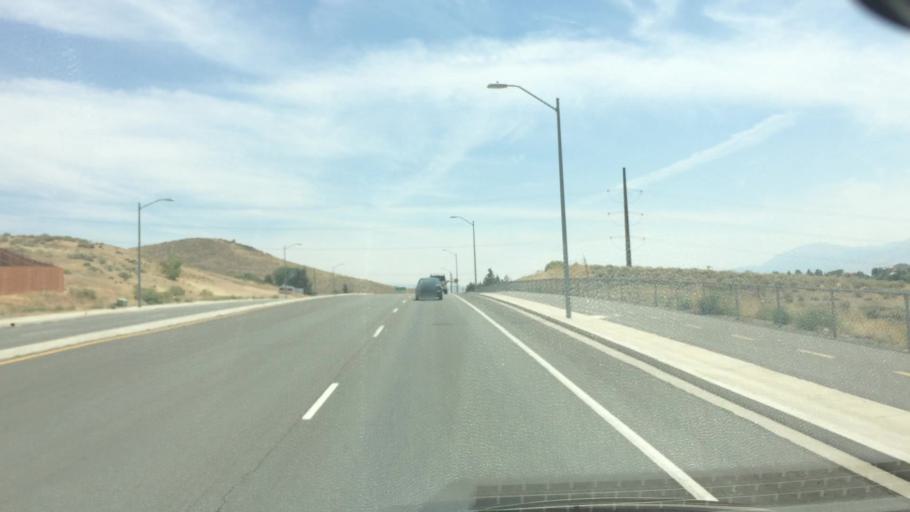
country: US
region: Nevada
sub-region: Washoe County
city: Sparks
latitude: 39.5729
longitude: -119.7242
